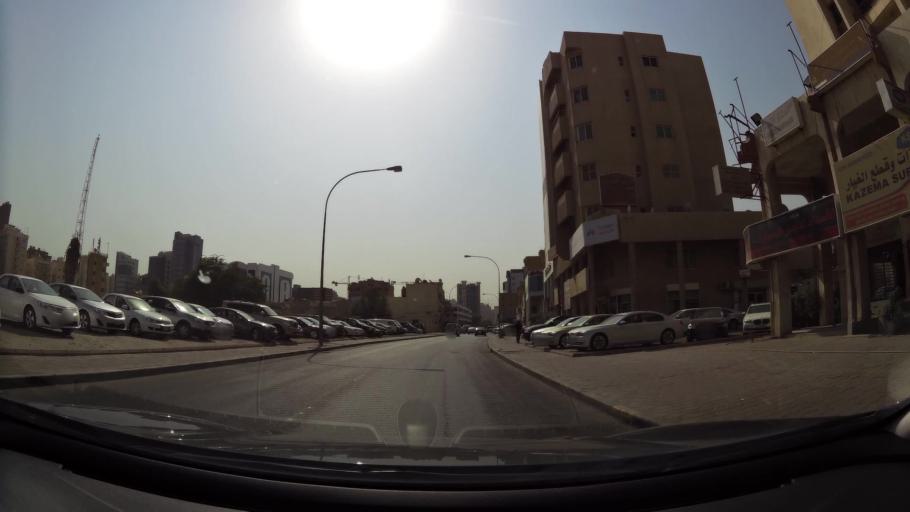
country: KW
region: Muhafazat Hawalli
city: Hawalli
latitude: 29.3375
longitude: 48.0164
